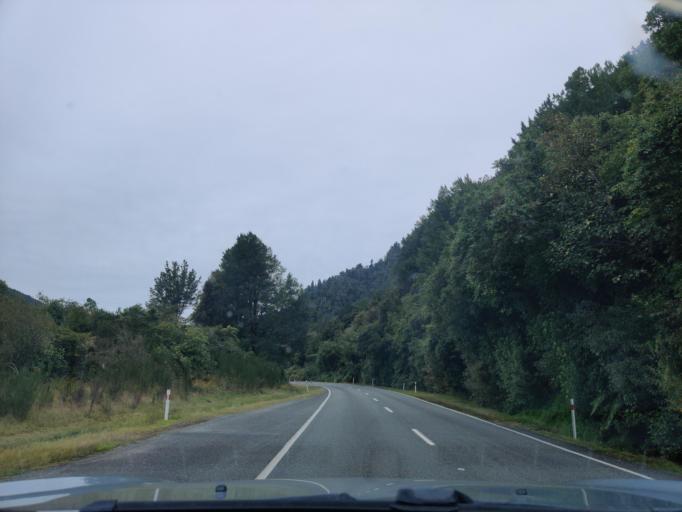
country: NZ
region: West Coast
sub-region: Buller District
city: Westport
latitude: -41.8514
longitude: 171.7439
